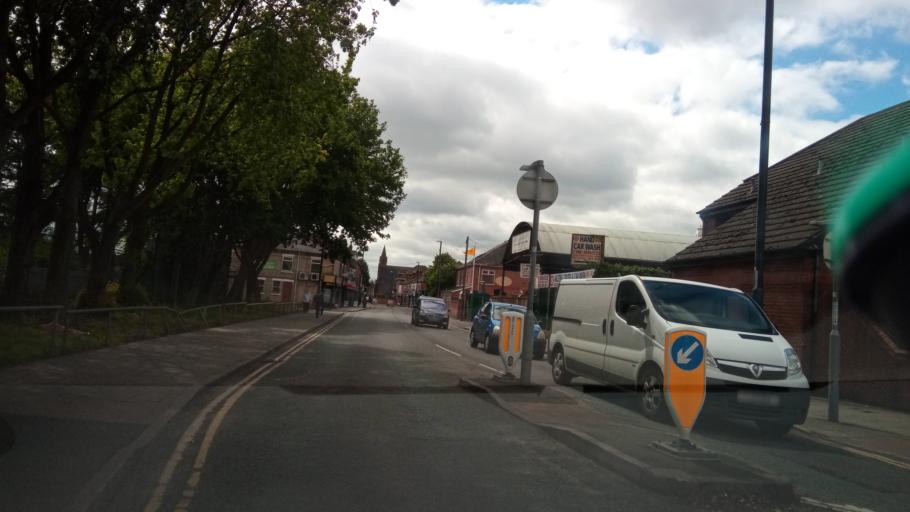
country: GB
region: England
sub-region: Derby
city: Derby
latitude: 52.9077
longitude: -1.4784
